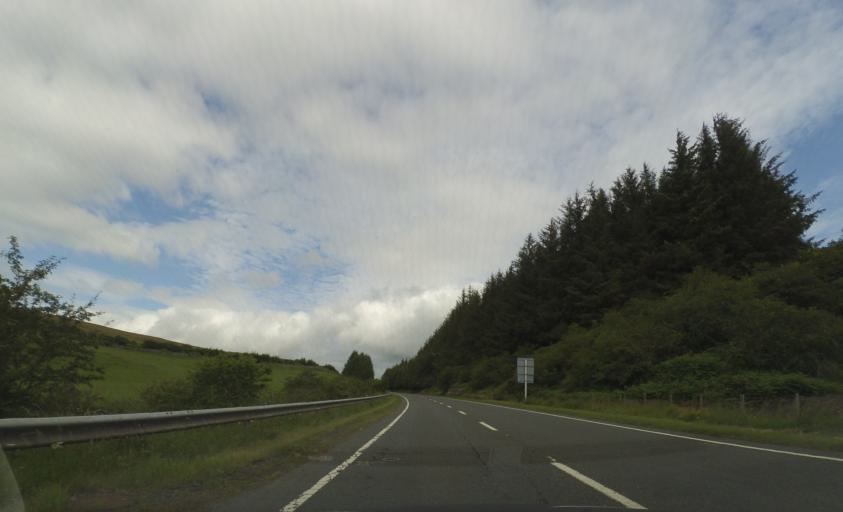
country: GB
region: Scotland
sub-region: The Scottish Borders
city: Selkirk
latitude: 55.5037
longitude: -2.8351
